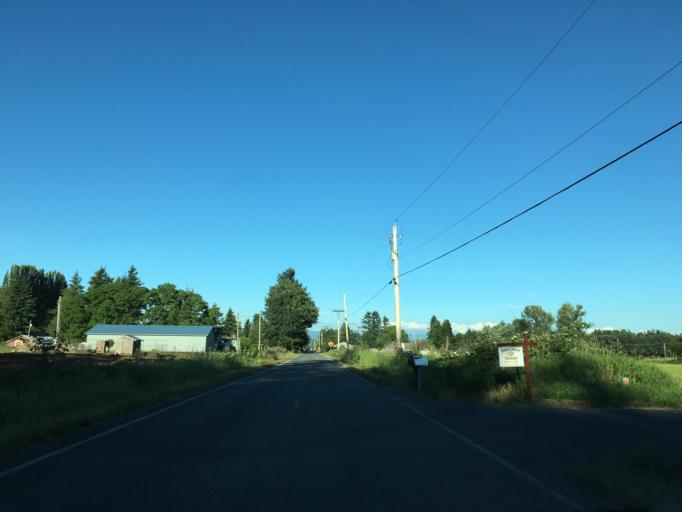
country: US
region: Washington
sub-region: Whatcom County
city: Ferndale
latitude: 48.9062
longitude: -122.5888
